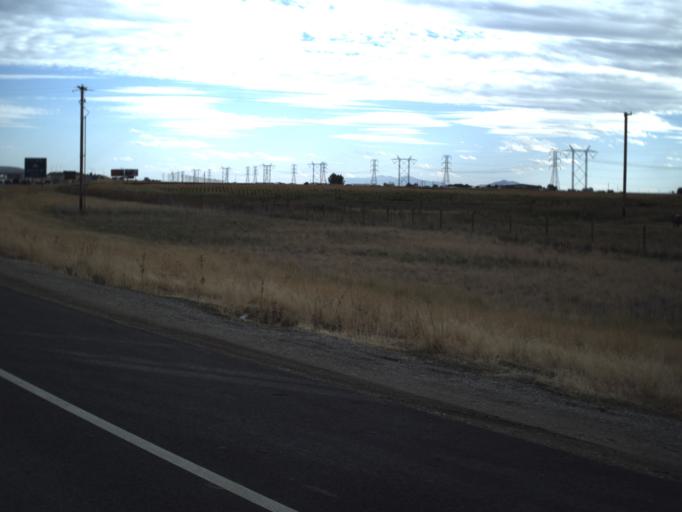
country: US
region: Utah
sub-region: Box Elder County
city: Brigham City
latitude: 41.5510
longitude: -112.0689
